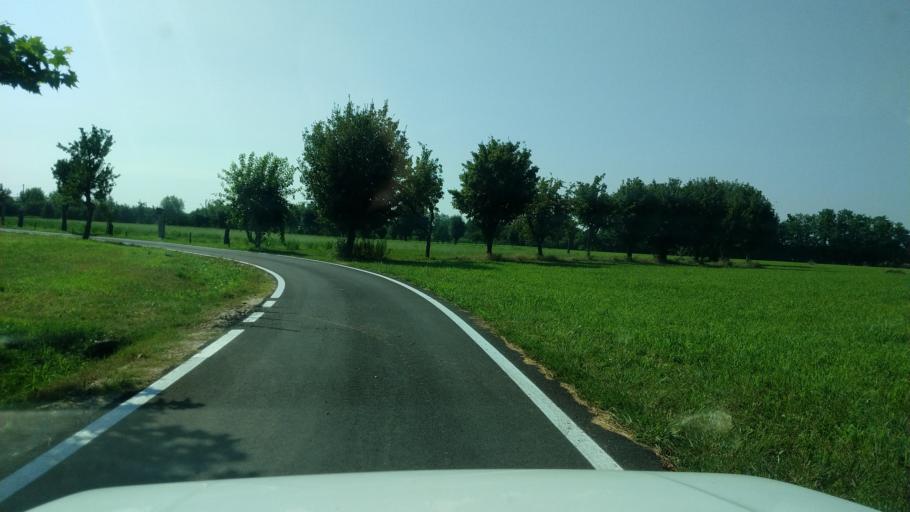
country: IT
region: Veneto
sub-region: Provincia di Vicenza
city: Schiavon
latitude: 45.7082
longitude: 11.6445
